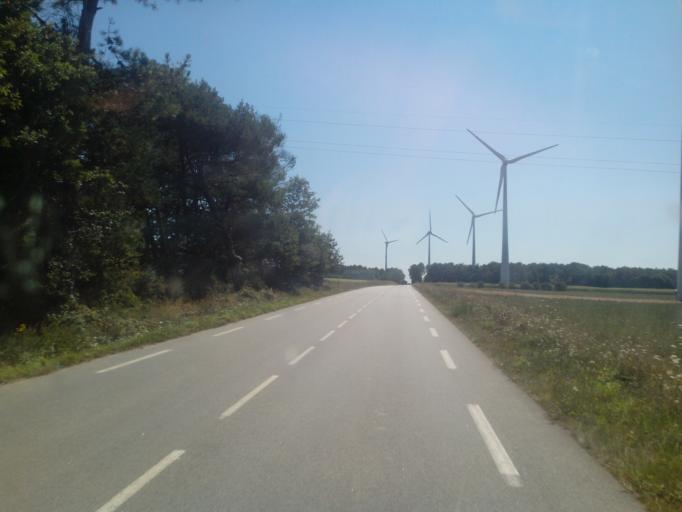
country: FR
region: Brittany
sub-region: Departement du Morbihan
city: Guillac
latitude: 47.8967
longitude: -2.5154
